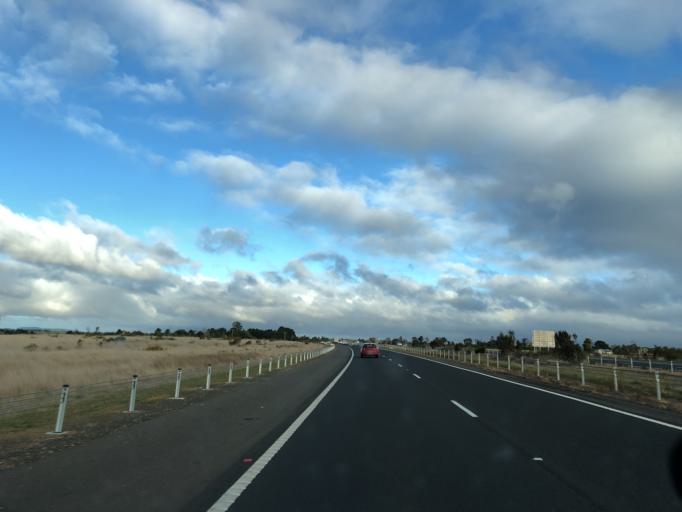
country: AU
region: Victoria
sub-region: Mount Alexander
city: Castlemaine
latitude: -37.2023
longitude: 144.4074
